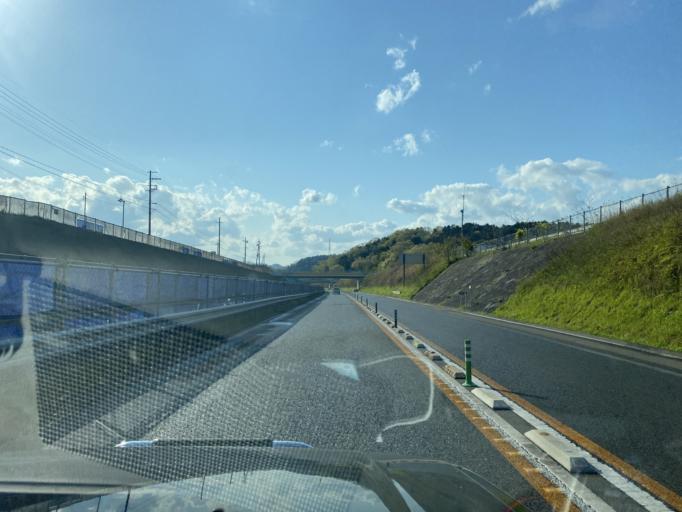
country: JP
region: Kyoto
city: Ayabe
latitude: 35.3263
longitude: 135.2345
